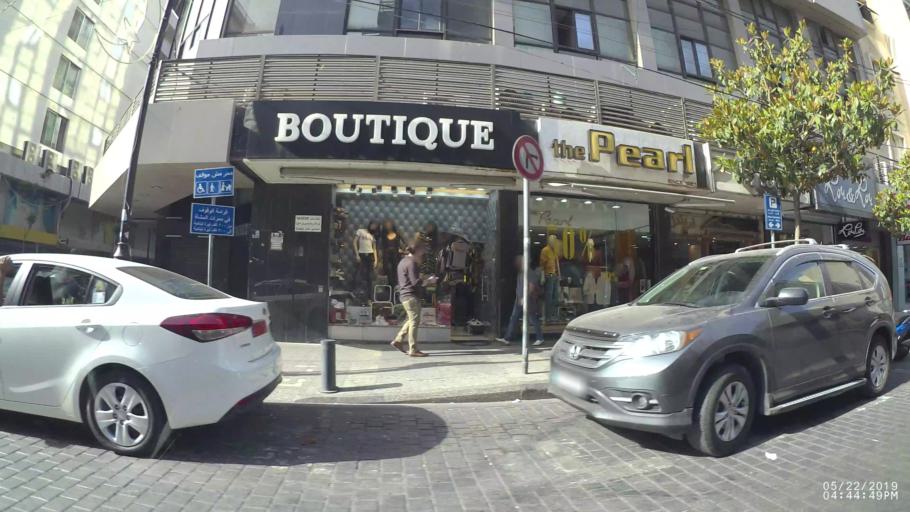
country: LB
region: Beyrouth
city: Ra's Bayrut
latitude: 33.8959
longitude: 35.4814
